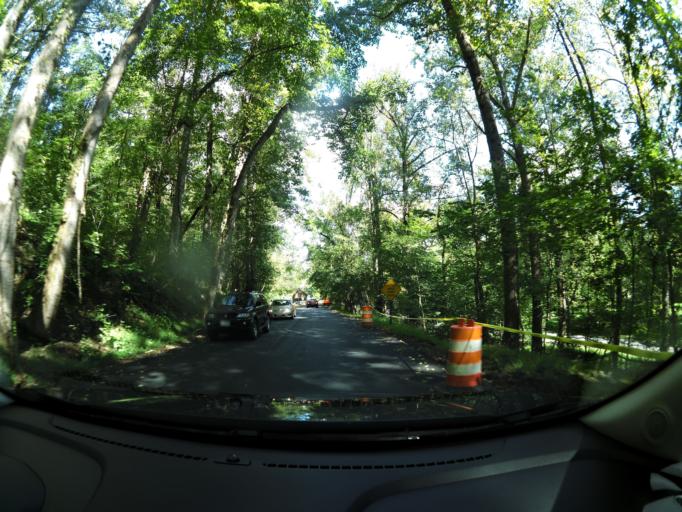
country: US
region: Virginia
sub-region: Fairfax County
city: Great Falls
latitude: 38.9942
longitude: -77.2555
